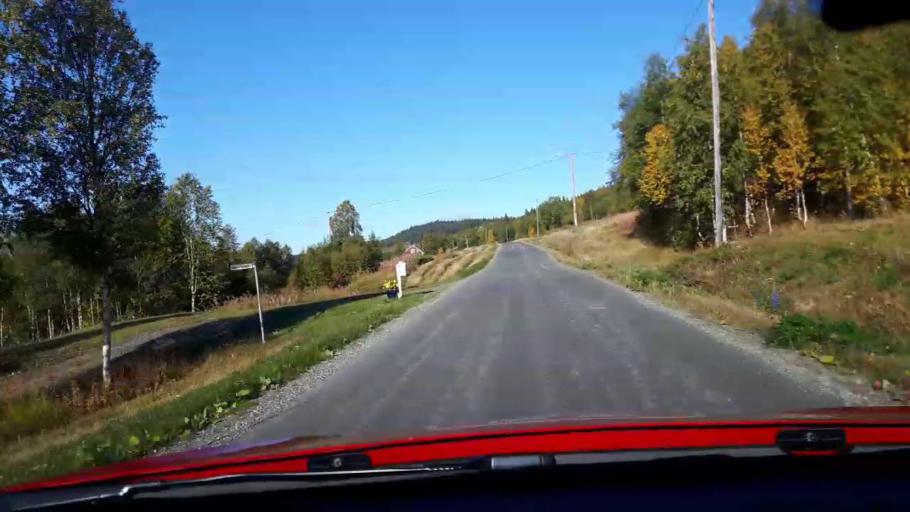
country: NO
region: Nord-Trondelag
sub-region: Lierne
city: Sandvika
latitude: 64.6063
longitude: 13.7793
